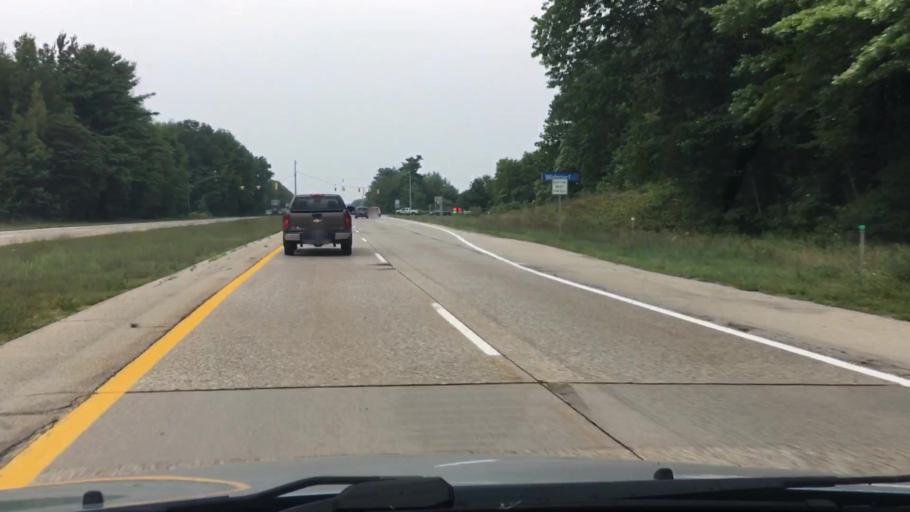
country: US
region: Michigan
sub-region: Ottawa County
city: Grand Haven
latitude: 43.0354
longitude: -86.2201
